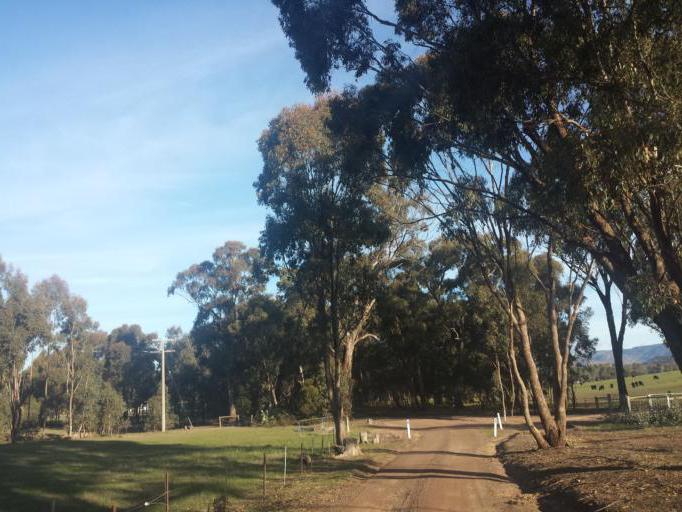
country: AU
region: Victoria
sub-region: Murrindindi
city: Kinglake West
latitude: -37.0255
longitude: 145.2320
